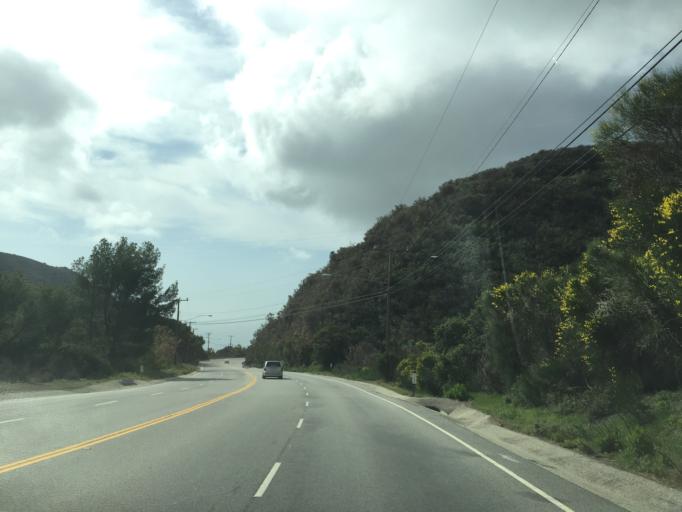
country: US
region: California
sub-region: Los Angeles County
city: Malibu
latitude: 34.0564
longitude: -118.7985
